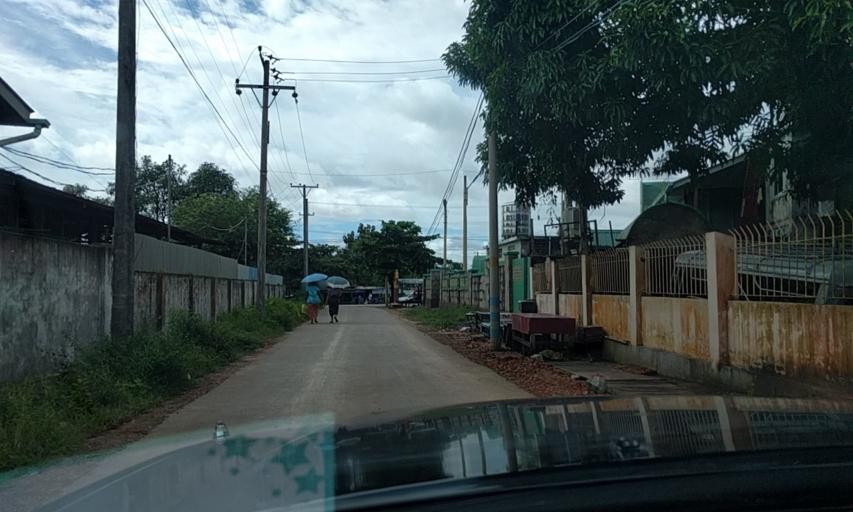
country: MM
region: Mon
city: Mawlamyine
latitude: 16.4599
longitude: 97.6486
